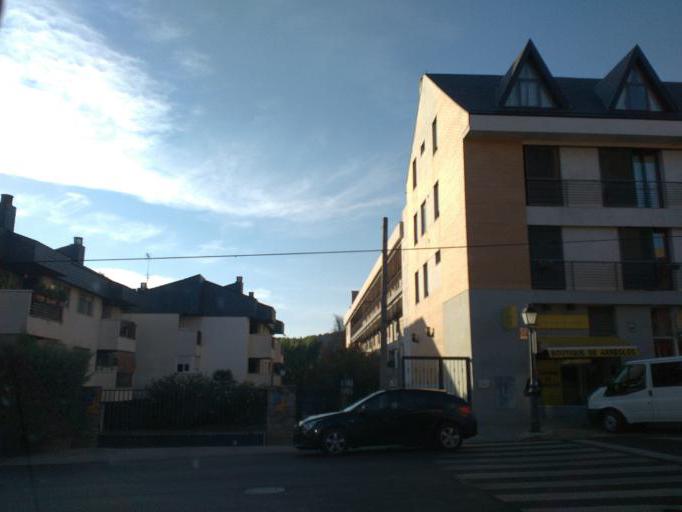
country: ES
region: Madrid
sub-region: Provincia de Madrid
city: Torrelodones
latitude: 40.5776
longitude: -3.9282
